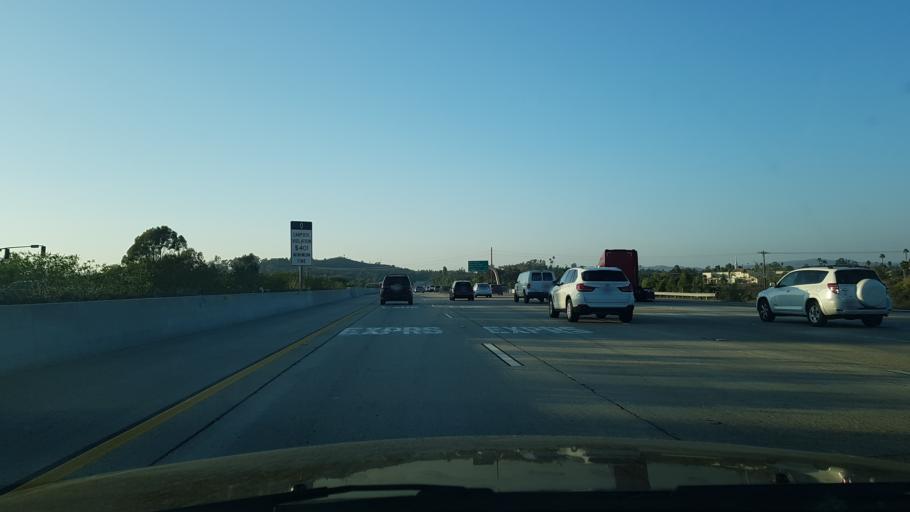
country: US
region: California
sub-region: San Diego County
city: Escondido
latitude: 33.0903
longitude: -117.0802
